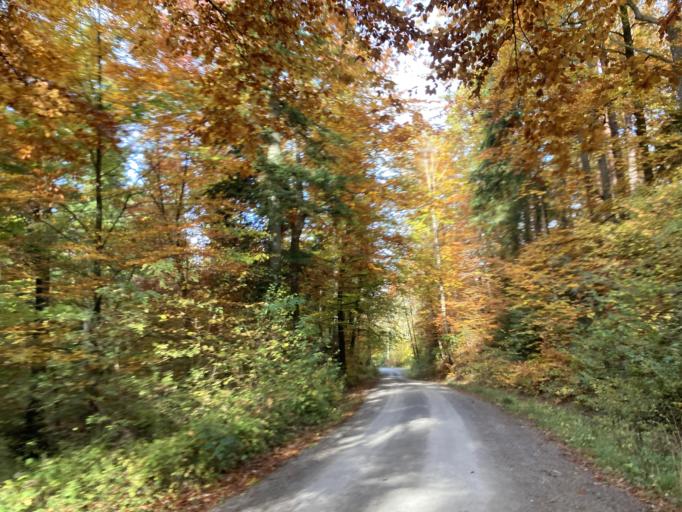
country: DE
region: Baden-Wuerttemberg
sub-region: Tuebingen Region
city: Rottenburg
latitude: 48.4511
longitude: 8.9470
